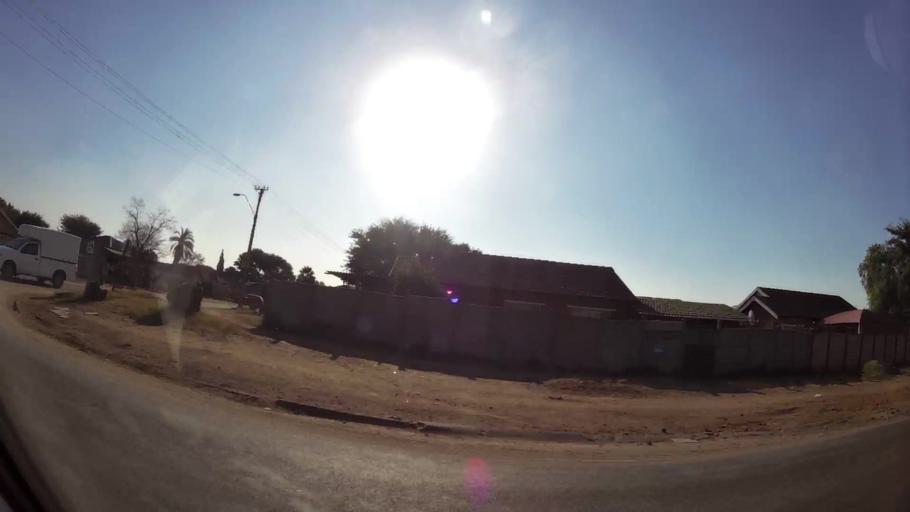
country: ZA
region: North-West
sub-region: Bojanala Platinum District Municipality
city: Rustenburg
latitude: -25.6538
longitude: 27.2582
